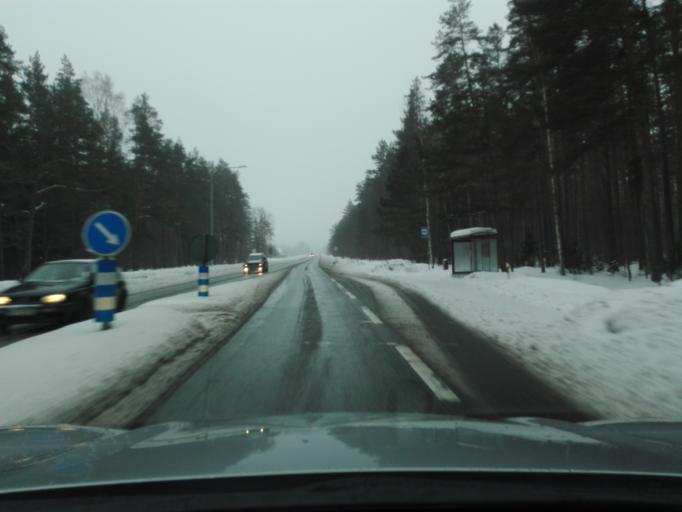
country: EE
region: Harju
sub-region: Kiili vald
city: Kiili
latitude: 59.3462
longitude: 24.7741
